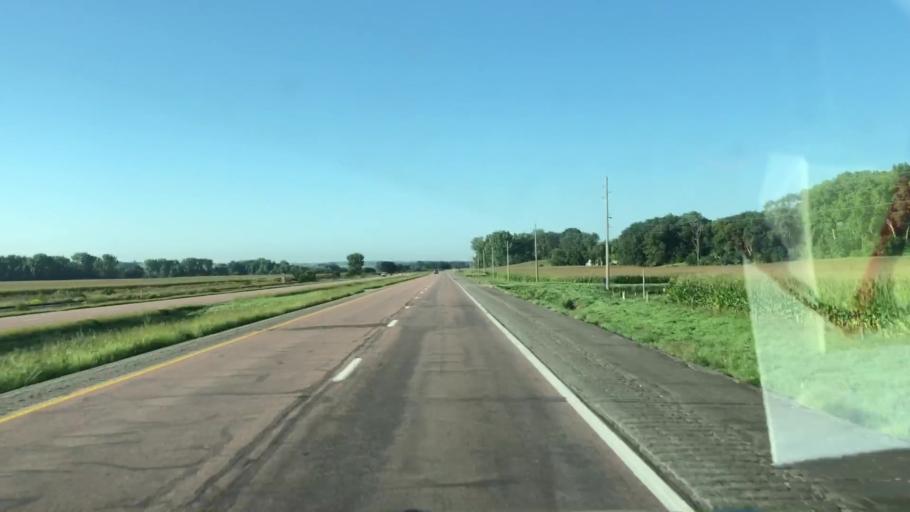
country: US
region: Iowa
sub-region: Woodbury County
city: Sioux City
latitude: 42.5913
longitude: -96.3066
